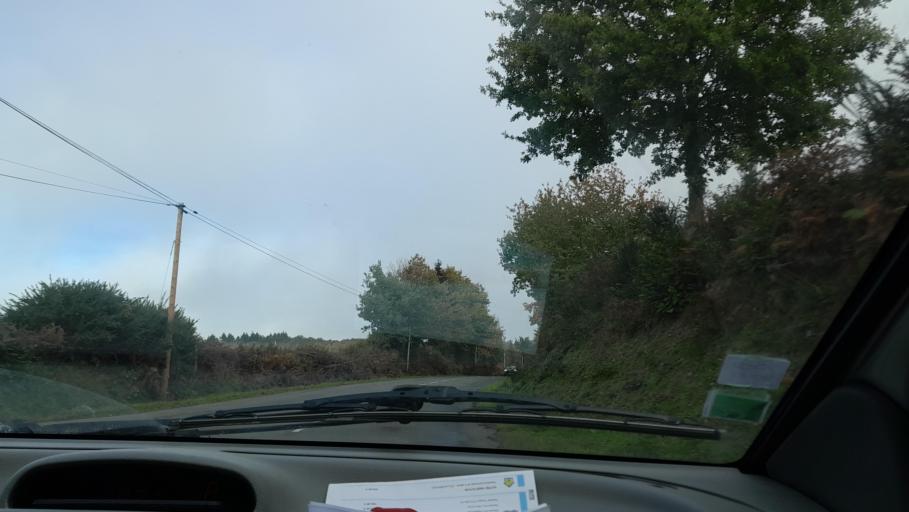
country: FR
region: Brittany
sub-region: Departement d'Ille-et-Vilaine
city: Luitre
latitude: 48.2716
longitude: -1.1483
